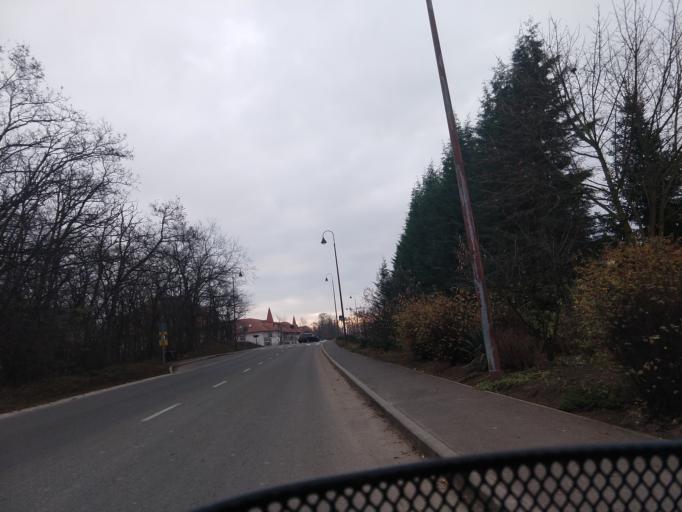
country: HU
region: Pest
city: Orbottyan
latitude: 47.6631
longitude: 19.2671
